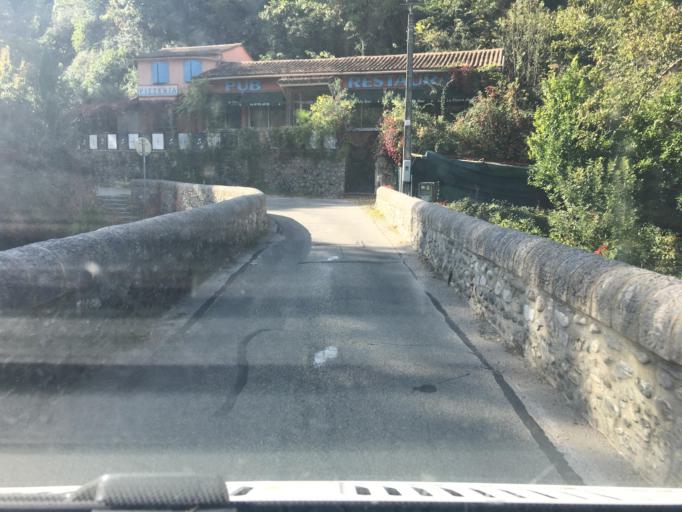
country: FR
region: Languedoc-Roussillon
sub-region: Departement du Gard
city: Sumene
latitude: 43.9658
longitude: 3.6872
